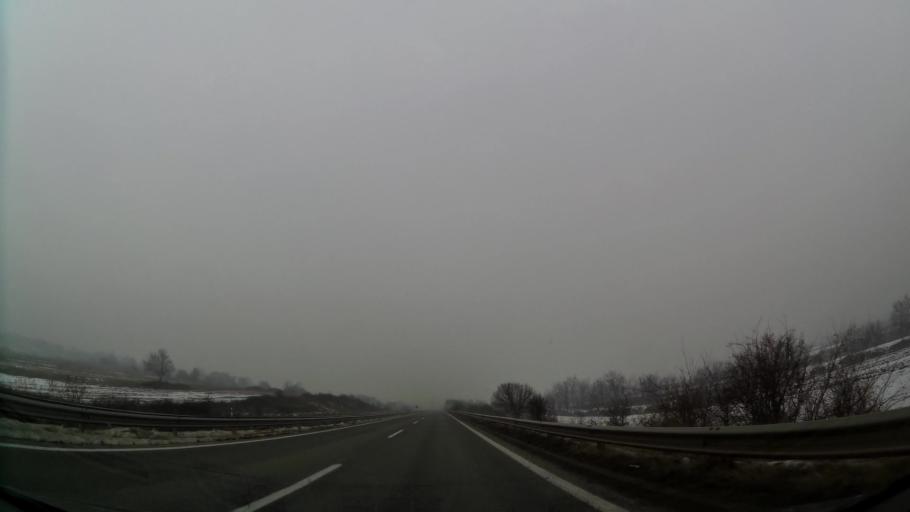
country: MK
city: Miladinovci
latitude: 41.9663
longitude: 21.6405
